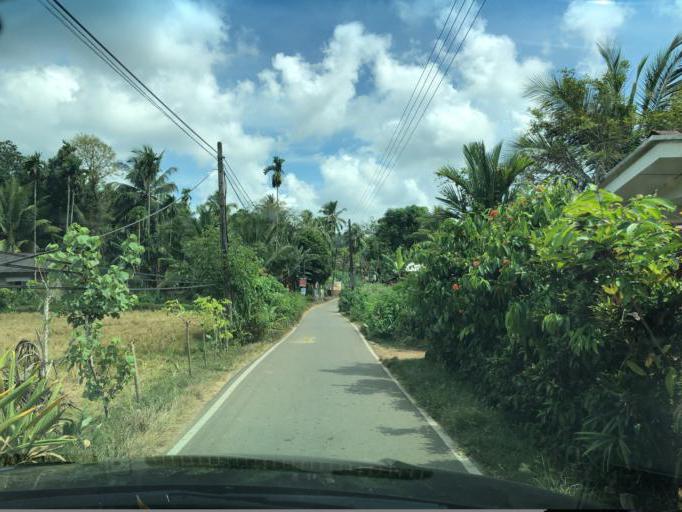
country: LK
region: Western
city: Horawala Junction
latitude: 6.5303
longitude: 80.0984
